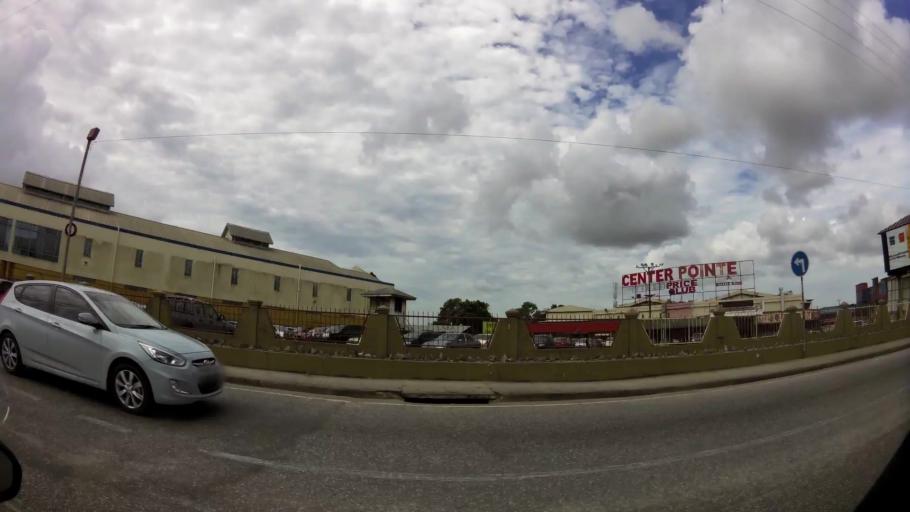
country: TT
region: Chaguanas
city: Chaguanas
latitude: 10.5120
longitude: -61.4090
